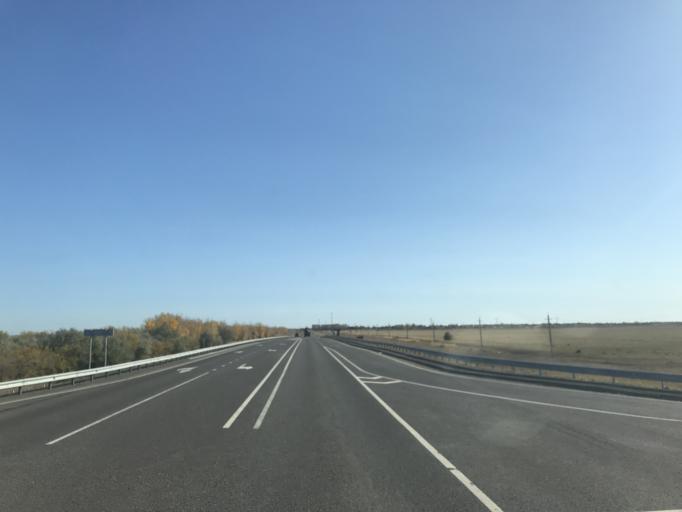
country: KZ
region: Pavlodar
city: Aksu
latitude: 51.9416
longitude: 77.3181
